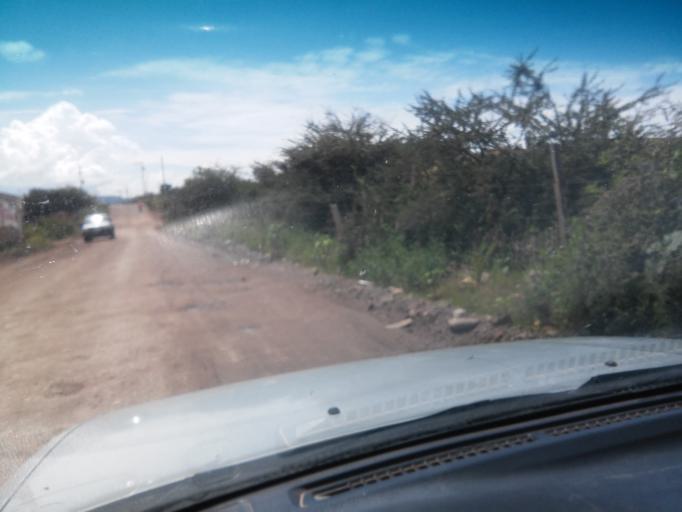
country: MX
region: Durango
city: Victoria de Durango
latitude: 23.9902
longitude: -104.7112
